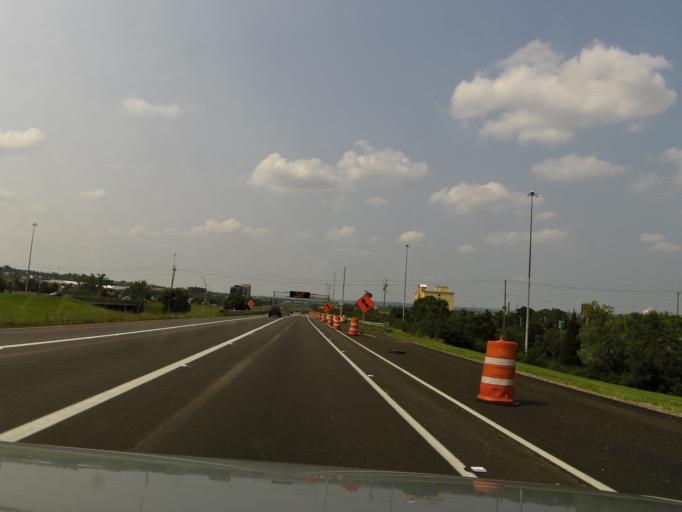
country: US
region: Ohio
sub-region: Hamilton County
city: Glendale
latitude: 39.2688
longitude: -84.4400
